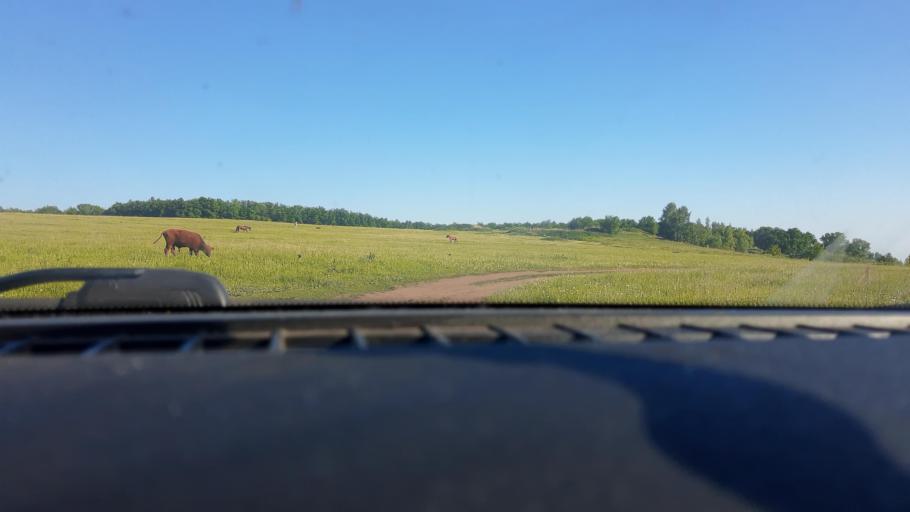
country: RU
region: Bashkortostan
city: Ulukulevo
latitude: 54.5532
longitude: 56.3236
